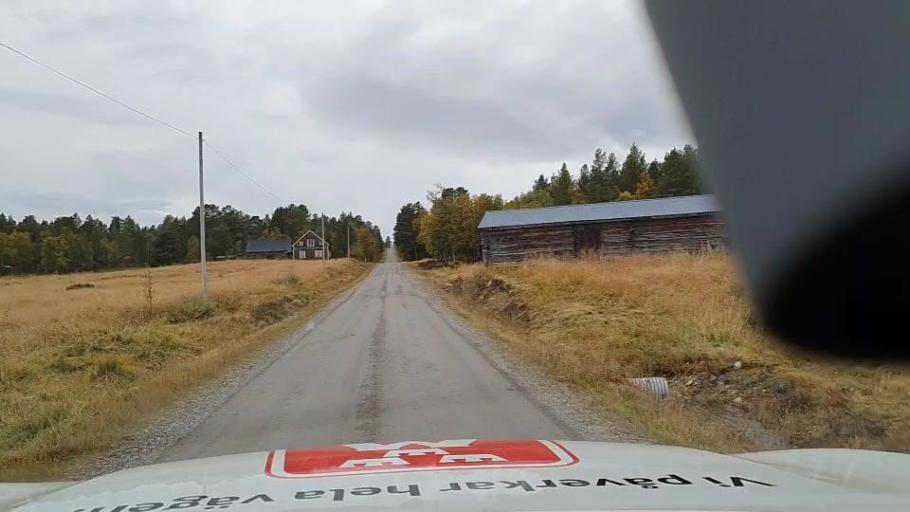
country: NO
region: Hedmark
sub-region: Engerdal
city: Engerdal
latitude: 62.1278
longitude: 12.8872
